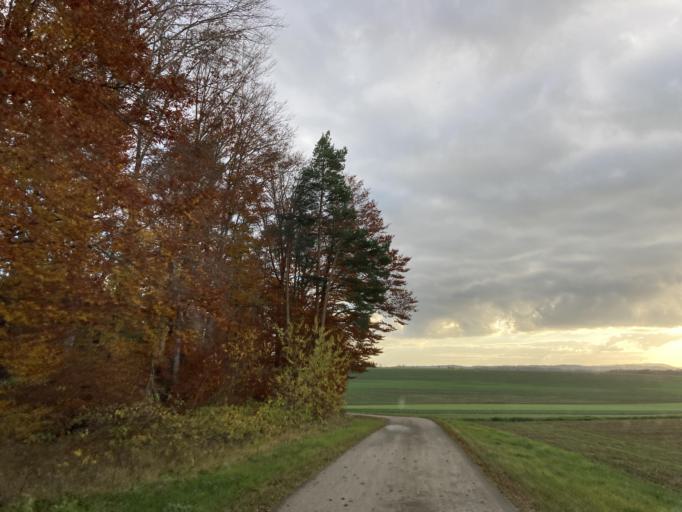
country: DE
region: Baden-Wuerttemberg
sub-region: Tuebingen Region
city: Haigerloch
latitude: 48.4200
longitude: 8.7860
